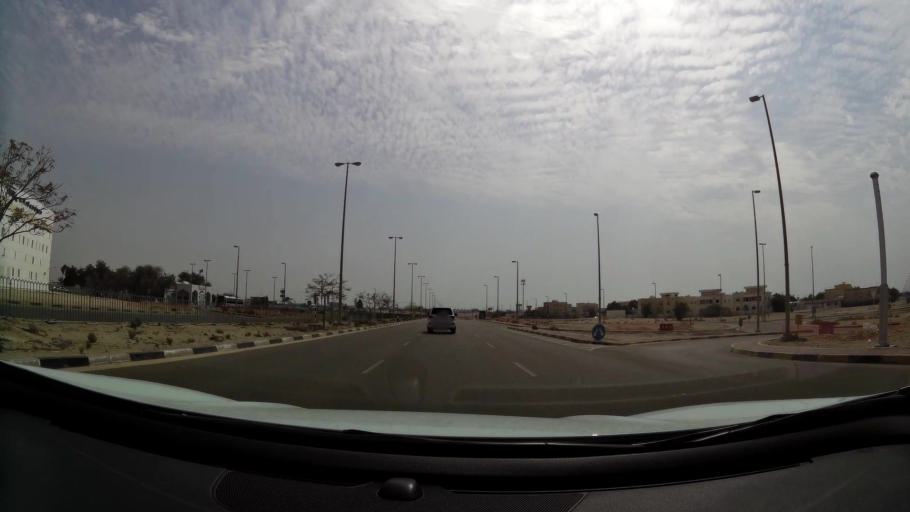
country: AE
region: Abu Dhabi
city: Abu Dhabi
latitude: 24.5493
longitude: 54.6848
